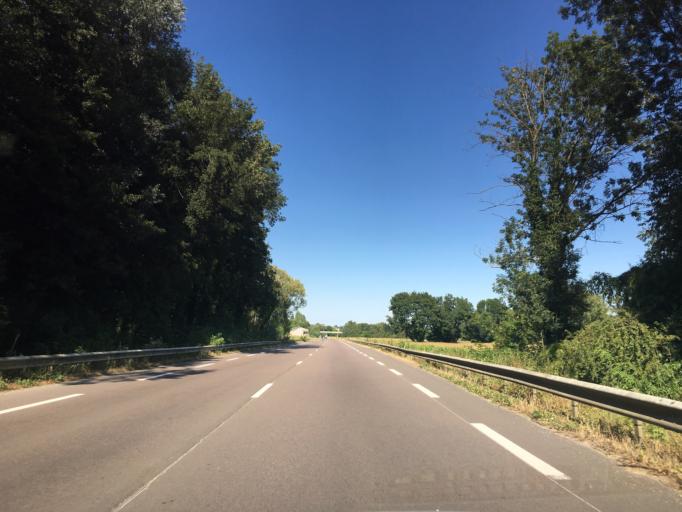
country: FR
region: Bourgogne
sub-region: Departement de l'Yonne
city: Maillot
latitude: 48.1809
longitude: 3.3016
